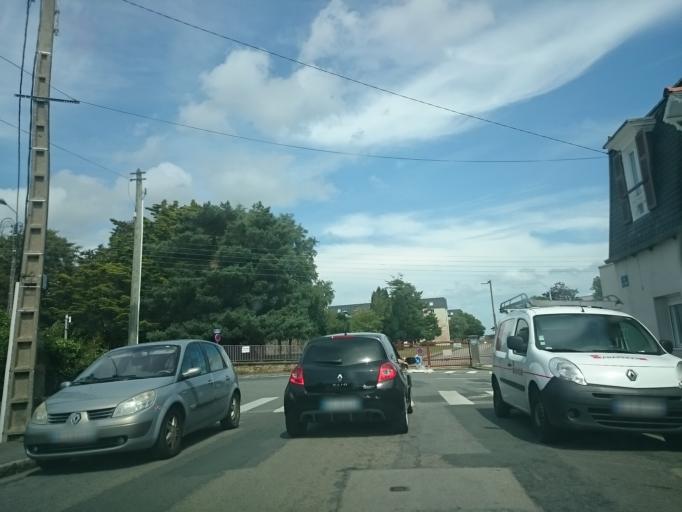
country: FR
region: Brittany
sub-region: Departement du Finistere
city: Brest
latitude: 48.4165
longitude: -4.4763
